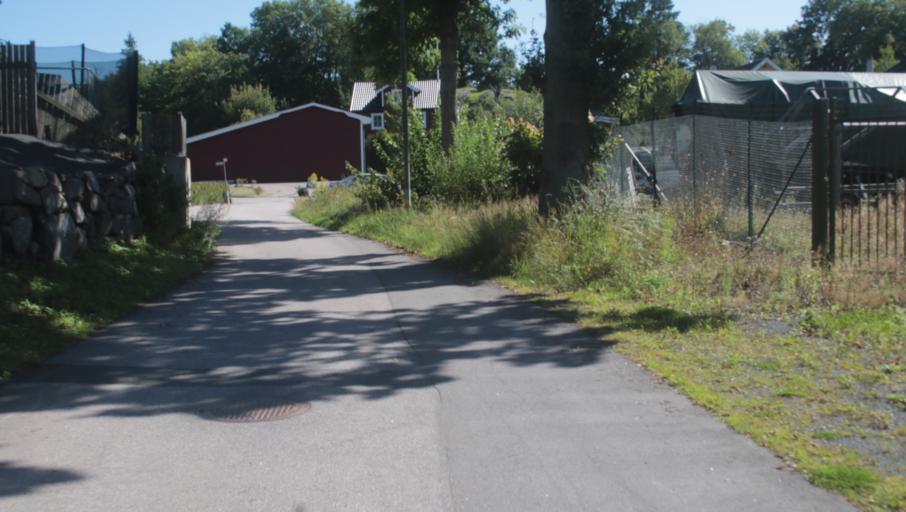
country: SE
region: Blekinge
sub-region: Karlshamns Kommun
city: Karlshamn
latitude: 56.1567
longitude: 14.8534
